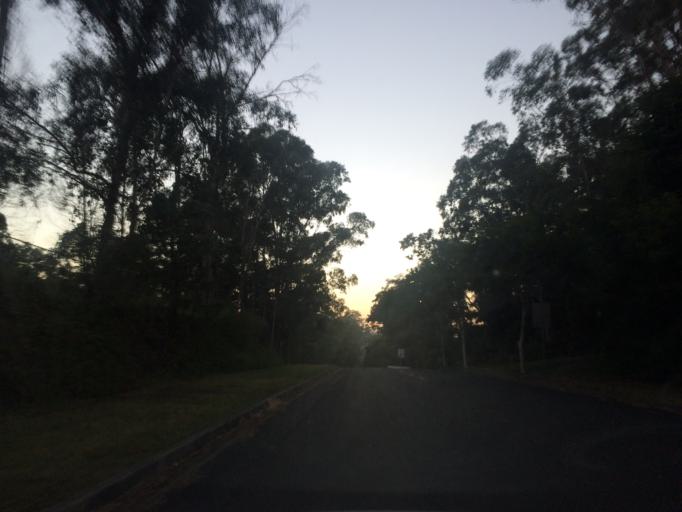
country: AU
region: Queensland
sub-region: Brisbane
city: Kenmore Hills
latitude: -27.5006
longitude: 152.9170
